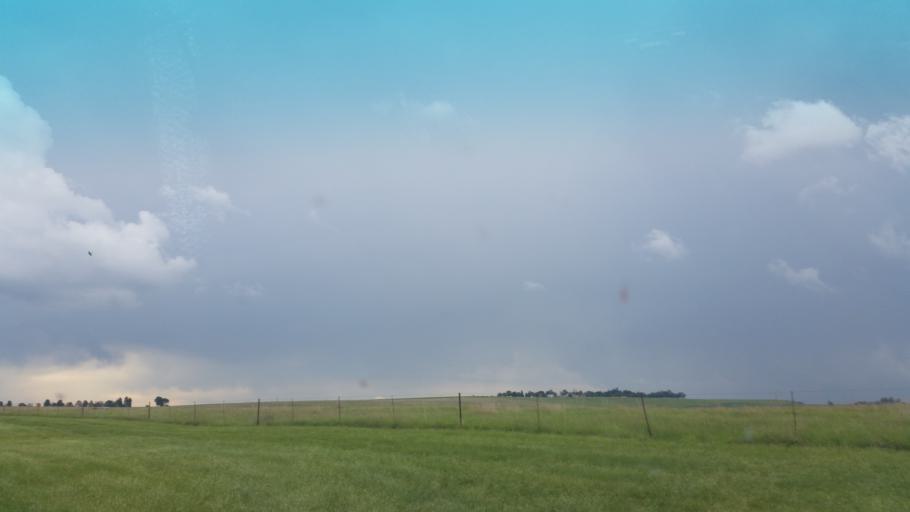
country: ZA
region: Orange Free State
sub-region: Thabo Mofutsanyana District Municipality
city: Harrismith
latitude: -28.1930
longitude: 29.0127
